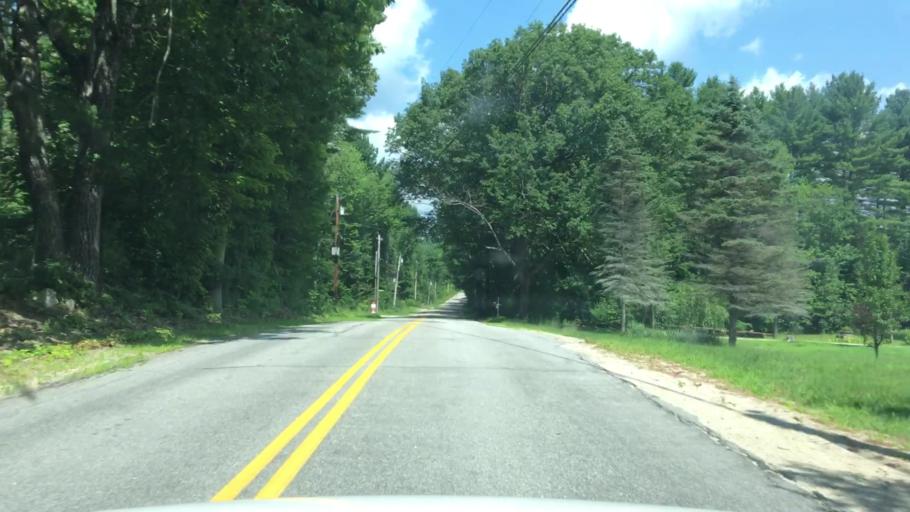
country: US
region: Maine
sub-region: Cumberland County
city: Raymond
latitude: 43.9483
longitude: -70.5255
